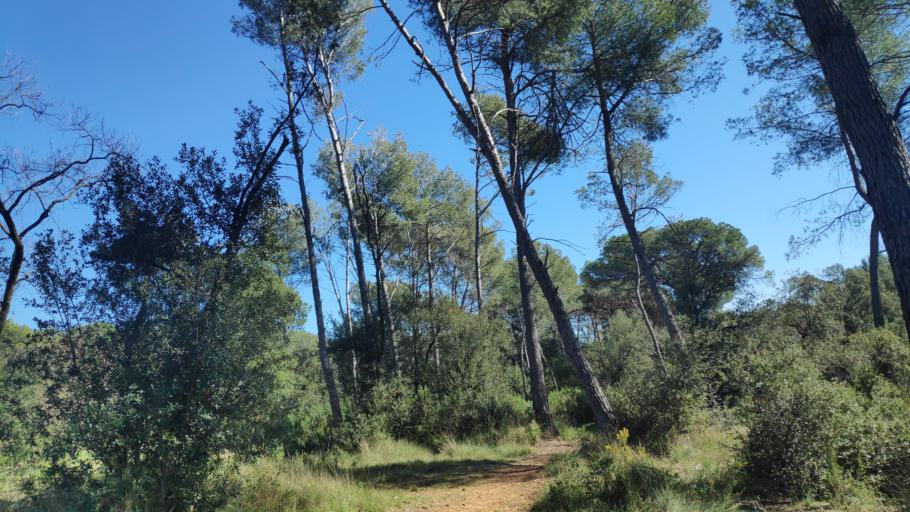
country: ES
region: Catalonia
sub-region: Provincia de Barcelona
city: Sant Quirze del Valles
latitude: 41.5639
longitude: 2.0644
